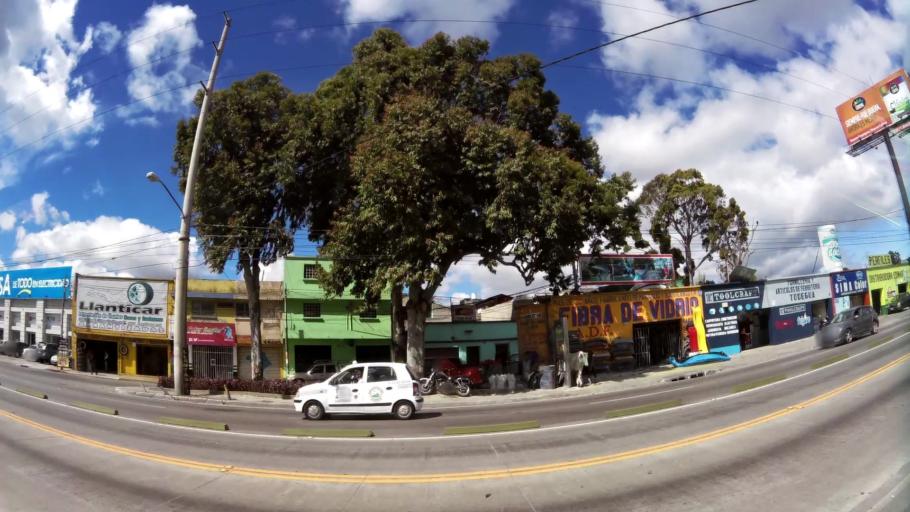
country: GT
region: Guatemala
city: Guatemala City
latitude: 14.6075
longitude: -90.5420
